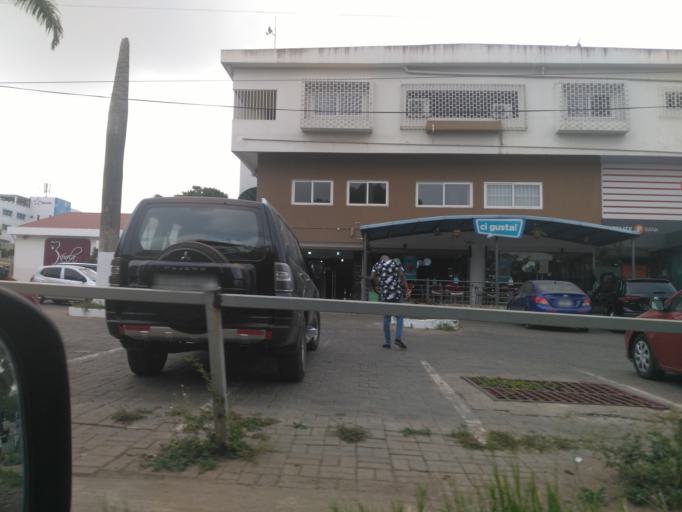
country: GH
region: Greater Accra
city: Accra
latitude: 5.6097
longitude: -0.1828
